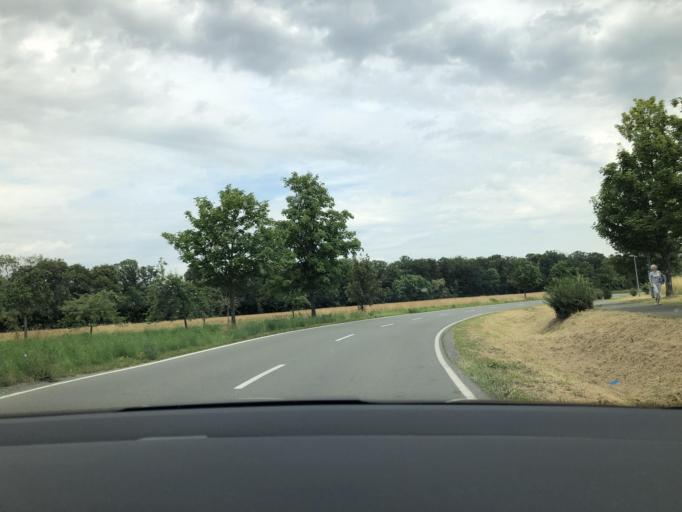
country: DE
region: Saxony-Anhalt
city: Blankenburg
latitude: 51.8087
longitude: 10.9280
